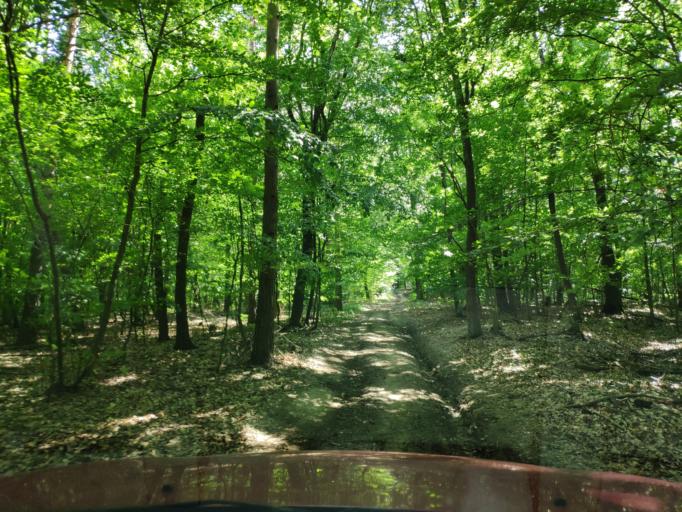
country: SK
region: Presovsky
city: Vranov nad Topl'ou
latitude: 48.8202
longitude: 21.6038
